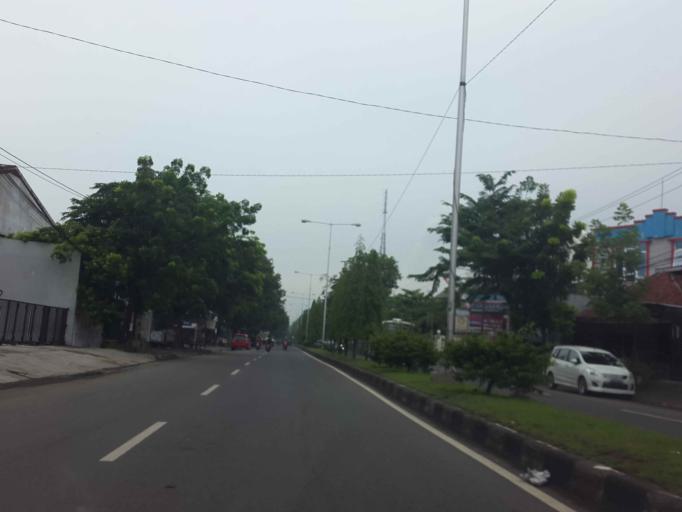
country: ID
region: Central Java
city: Semarang
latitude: -6.9986
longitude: 110.4646
